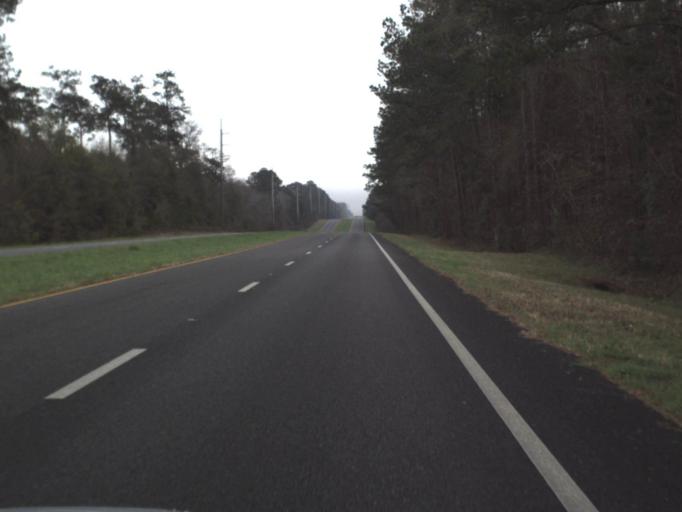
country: US
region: Florida
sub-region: Leon County
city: Woodville
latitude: 30.4023
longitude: -84.0460
